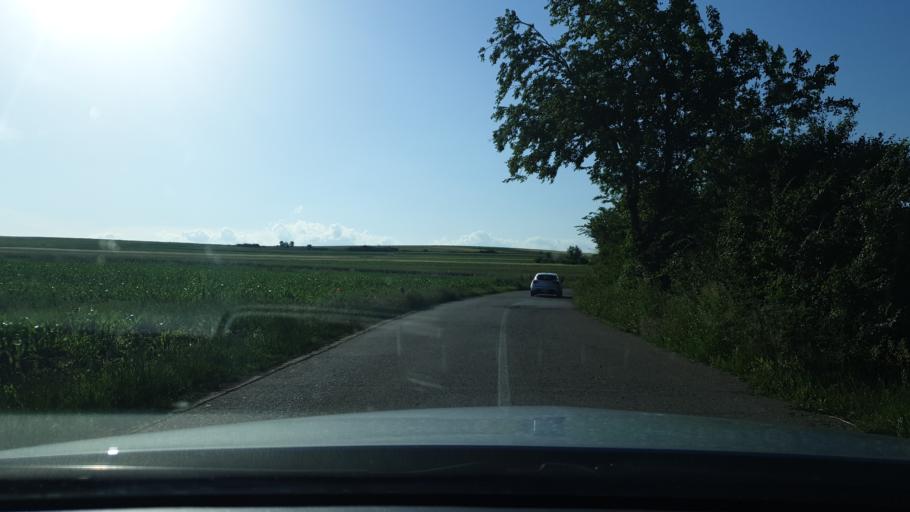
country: RS
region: Central Serbia
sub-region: Nisavski Okrug
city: Aleksinac
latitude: 43.6168
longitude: 21.6831
